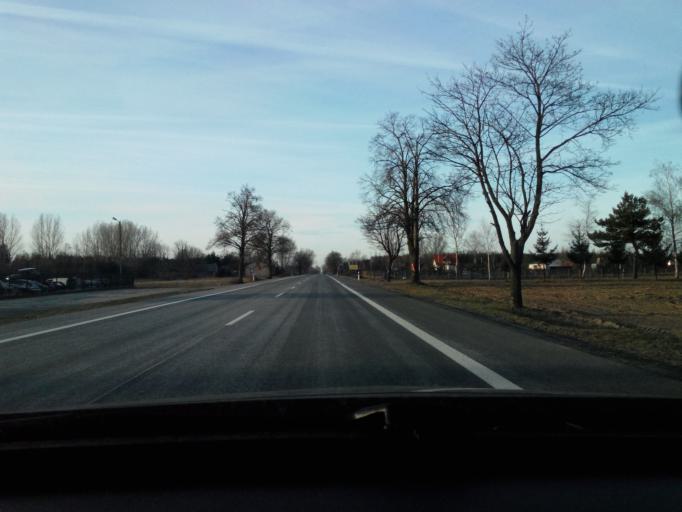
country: PL
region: Kujawsko-Pomorskie
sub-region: Powiat wloclawski
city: Lubien Kujawski
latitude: 52.4155
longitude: 19.1660
